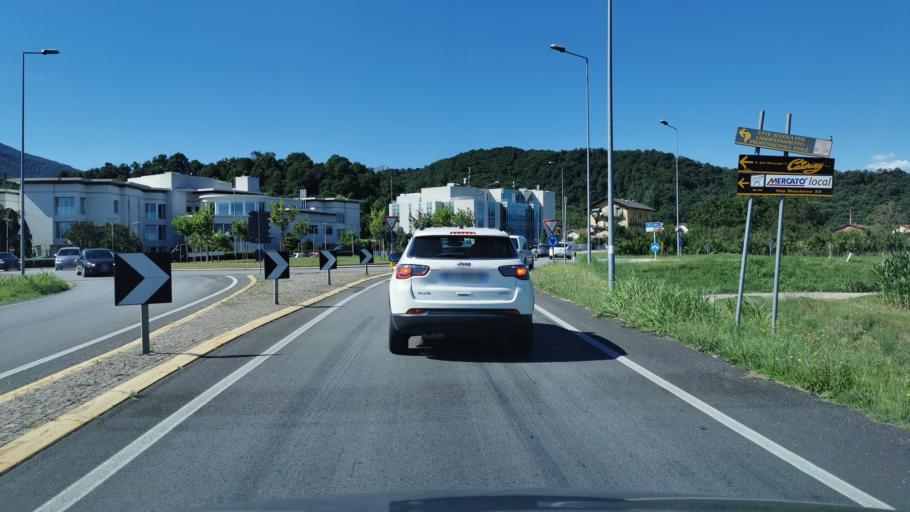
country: IT
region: Piedmont
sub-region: Provincia di Cuneo
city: Boves
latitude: 44.3385
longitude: 7.5441
